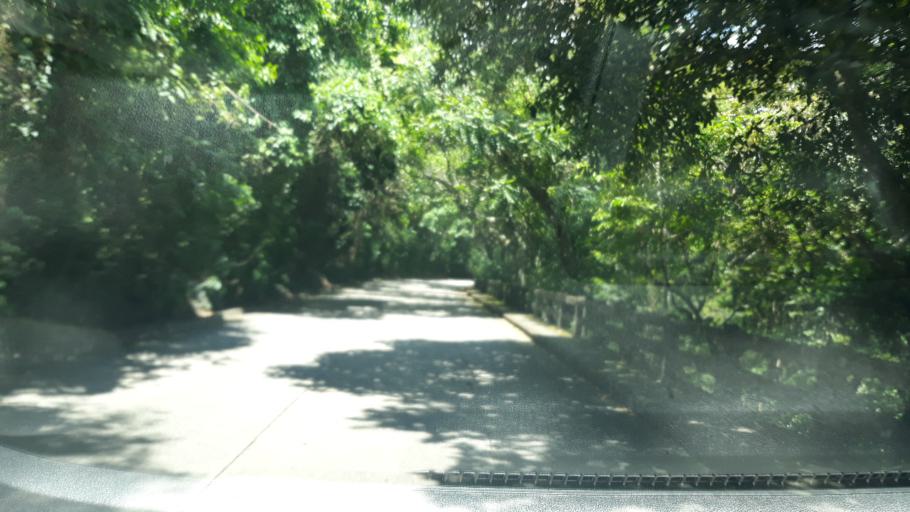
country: BR
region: Rio de Janeiro
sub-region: Rio De Janeiro
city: Rio de Janeiro
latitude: -22.9483
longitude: -43.2077
